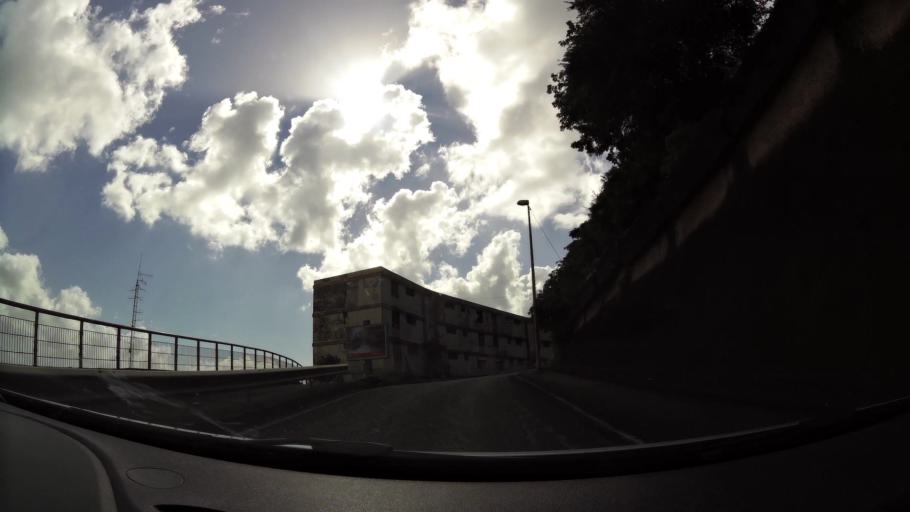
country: MQ
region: Martinique
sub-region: Martinique
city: Fort-de-France
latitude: 14.6143
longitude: -61.0638
